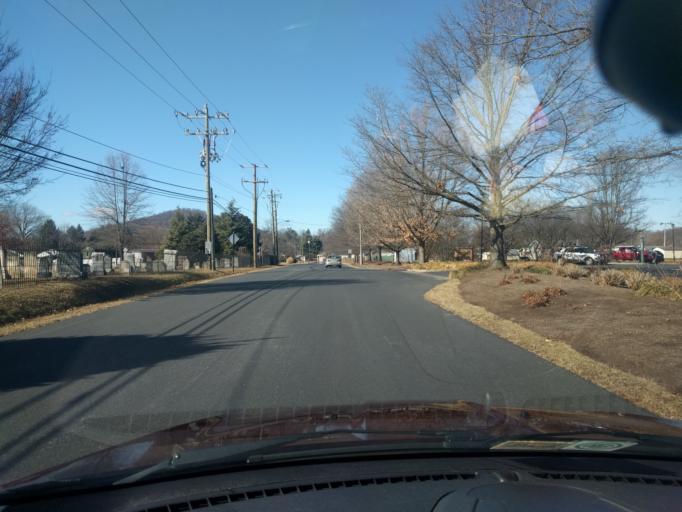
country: US
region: Virginia
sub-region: Rockingham County
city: Bridgewater
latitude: 38.3851
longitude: -78.9748
